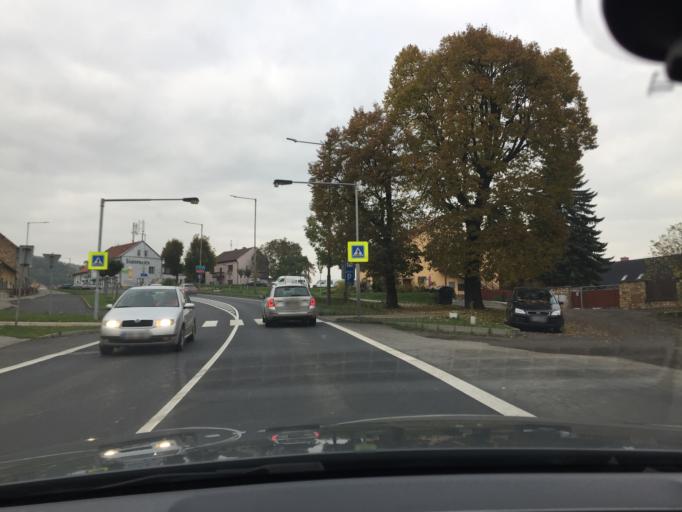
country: CZ
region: Ustecky
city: Velemin
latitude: 50.5401
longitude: 13.9783
